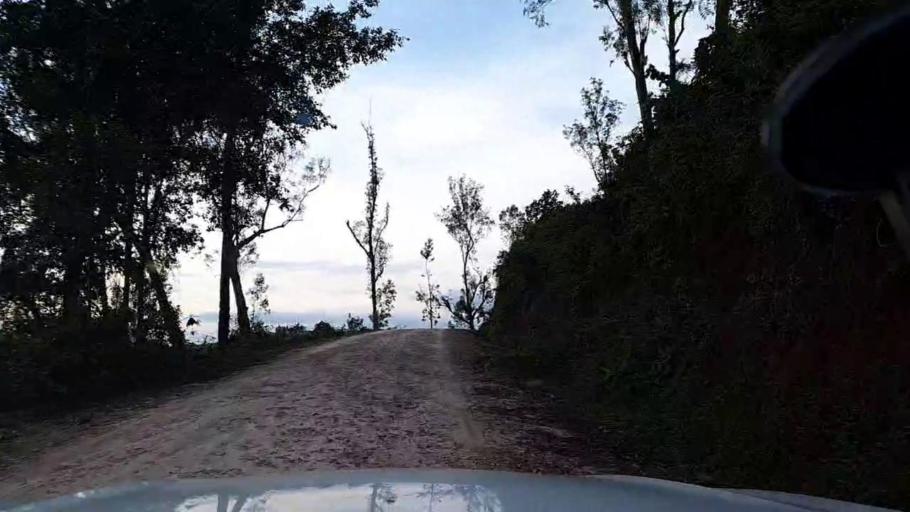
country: RW
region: Southern Province
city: Nyanza
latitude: -2.2141
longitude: 29.6269
